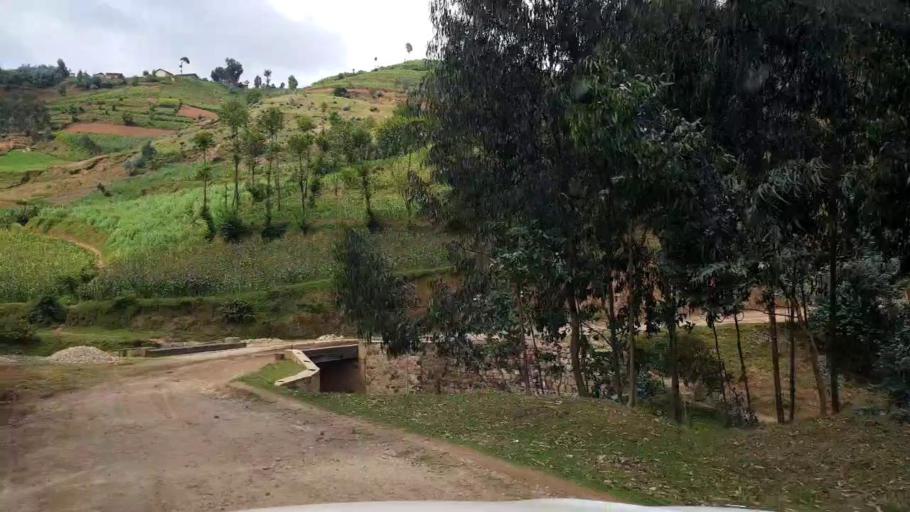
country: RW
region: Western Province
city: Kibuye
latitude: -1.8927
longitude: 29.4625
